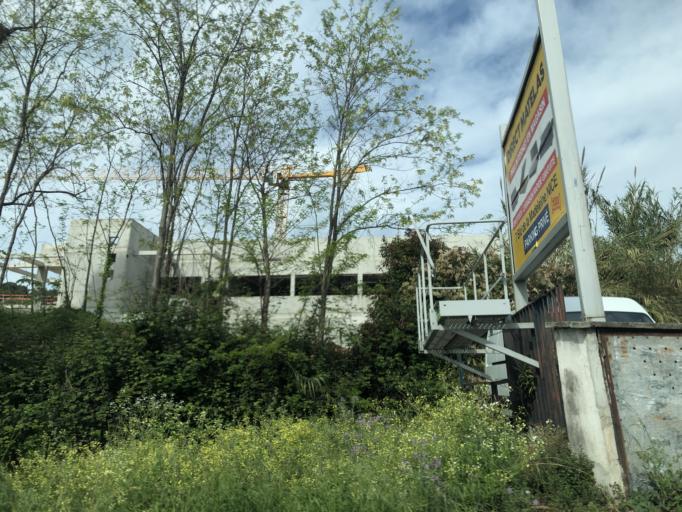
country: FR
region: Provence-Alpes-Cote d'Azur
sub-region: Departement des Alpes-Maritimes
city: Saint-Laurent-du-Var
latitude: 43.6902
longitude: 7.1855
